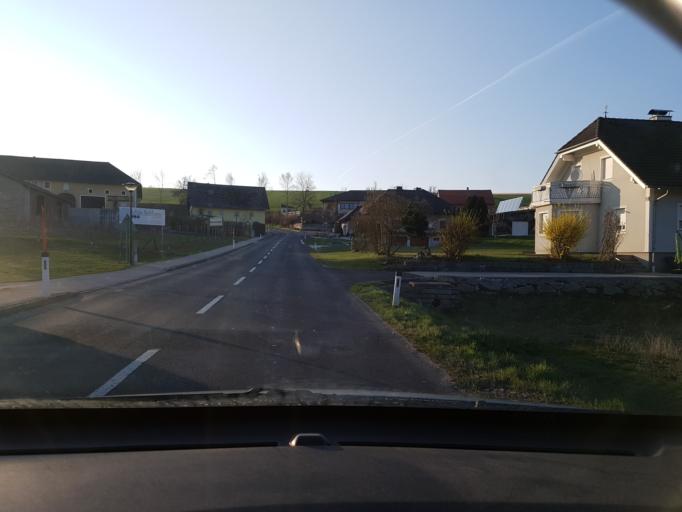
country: AT
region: Upper Austria
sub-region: Politischer Bezirk Linz-Land
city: Sankt Florian
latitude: 48.1643
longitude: 14.3366
